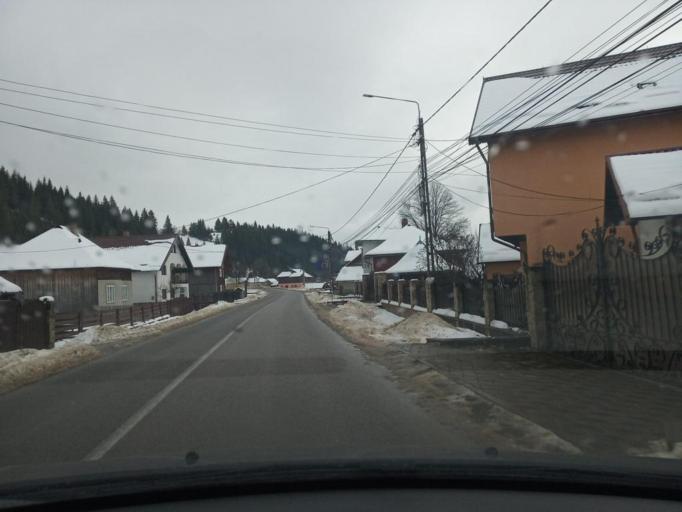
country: RO
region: Suceava
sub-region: Comuna Manastirea Humorului
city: Manastirea Humorului
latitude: 47.5910
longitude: 25.8655
